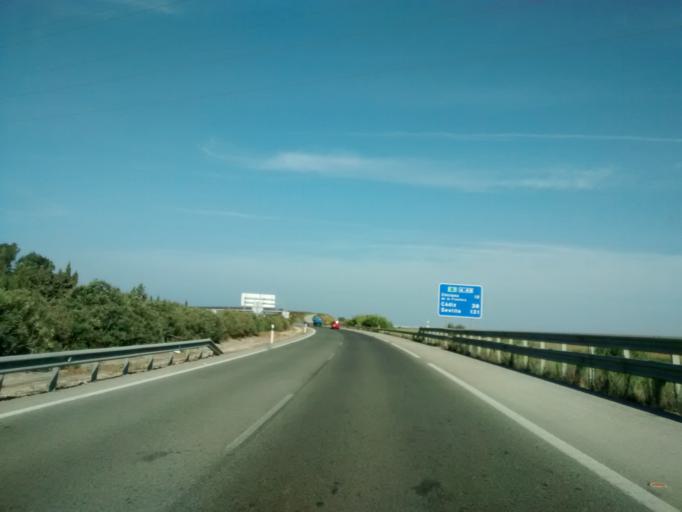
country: ES
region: Andalusia
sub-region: Provincia de Cadiz
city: Conil de la Frontera
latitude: 36.3508
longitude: -6.0671
